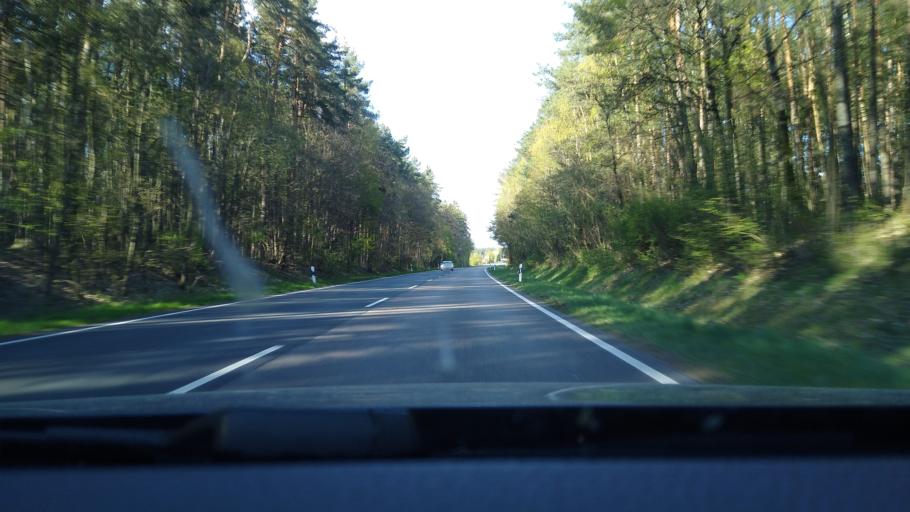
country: DE
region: Bavaria
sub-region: Regierungsbezirk Mittelfranken
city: Abenberg
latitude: 49.2556
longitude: 10.9028
